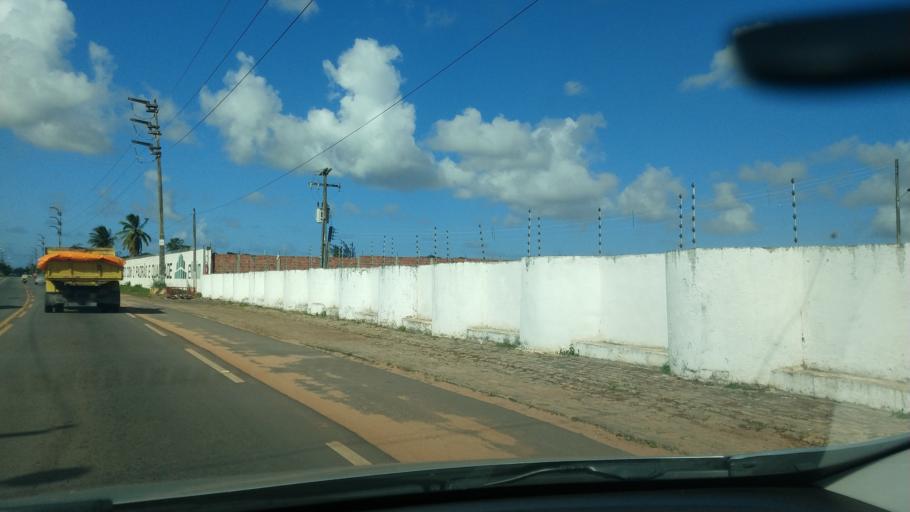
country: BR
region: Rio Grande do Norte
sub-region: Sao Goncalo Do Amarante
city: Sao Goncalo do Amarante
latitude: -5.7884
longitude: -35.2972
